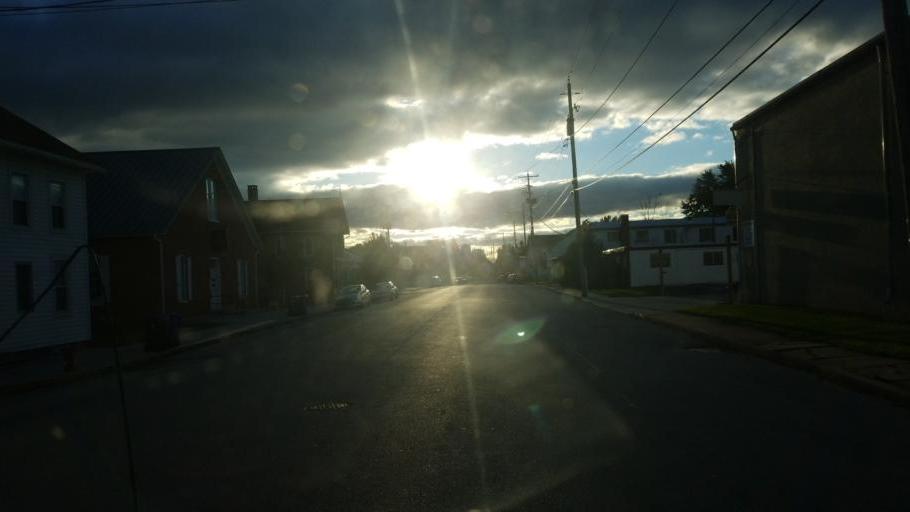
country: US
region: Pennsylvania
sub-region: Adams County
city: East Berlin
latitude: 39.9370
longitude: -76.9810
